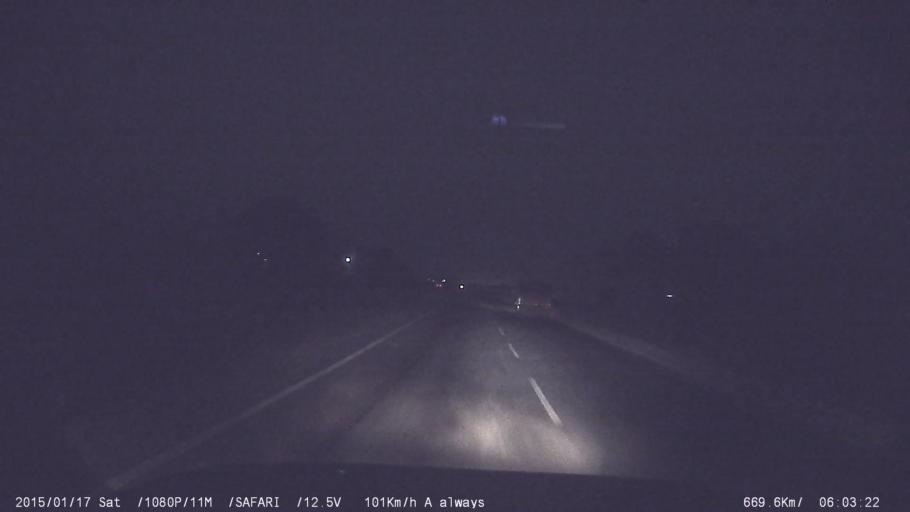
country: IN
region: Tamil Nadu
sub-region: Kancheepuram
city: Kanchipuram
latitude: 12.8817
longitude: 79.6021
